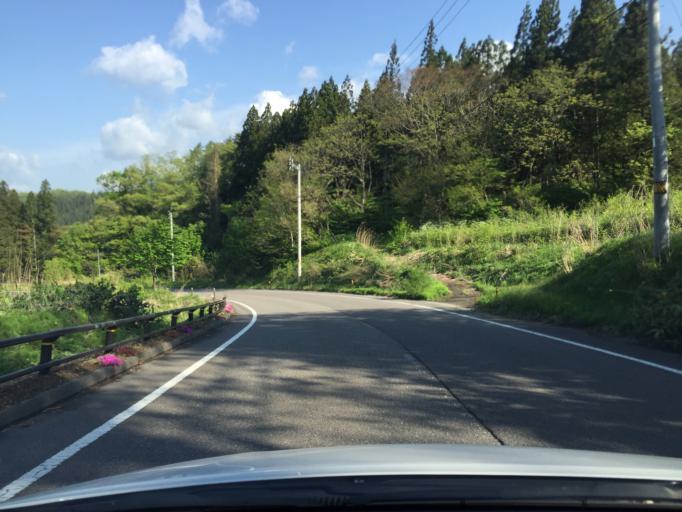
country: JP
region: Fukushima
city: Kitakata
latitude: 37.6864
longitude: 139.6738
